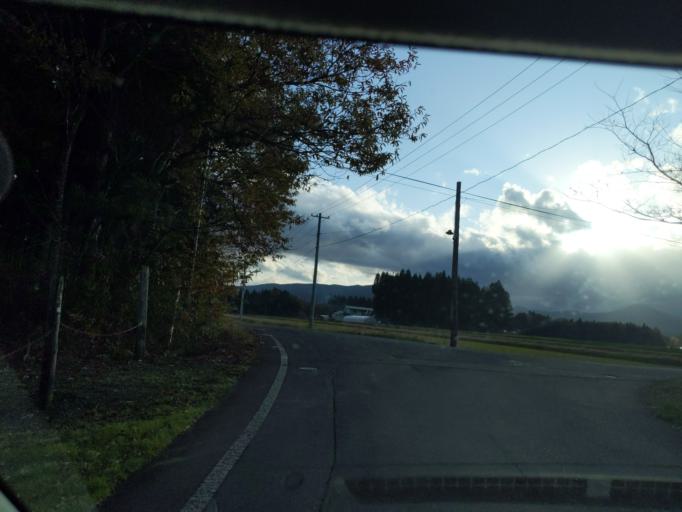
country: JP
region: Iwate
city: Mizusawa
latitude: 39.1068
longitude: 140.9990
